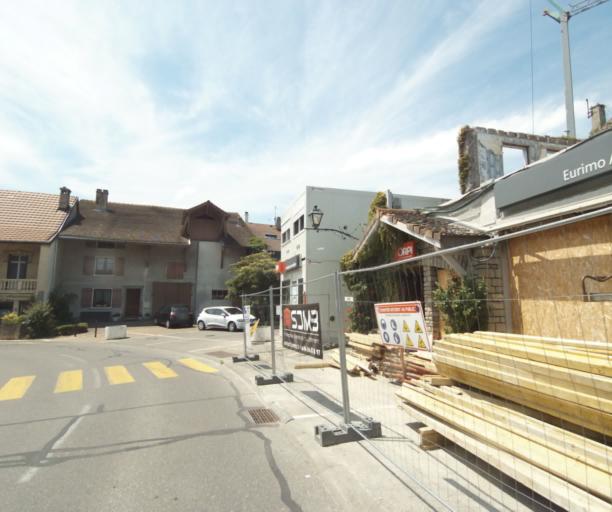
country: FR
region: Rhone-Alpes
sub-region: Departement de la Haute-Savoie
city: Messery
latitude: 46.3508
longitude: 6.2919
